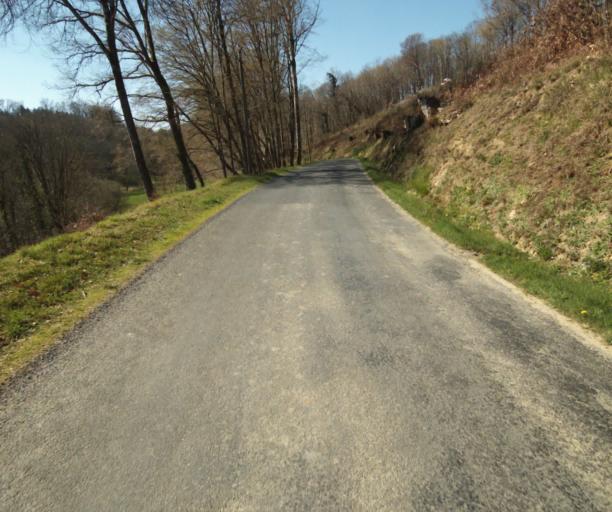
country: FR
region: Limousin
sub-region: Departement de la Correze
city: Chameyrat
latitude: 45.2570
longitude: 1.7205
